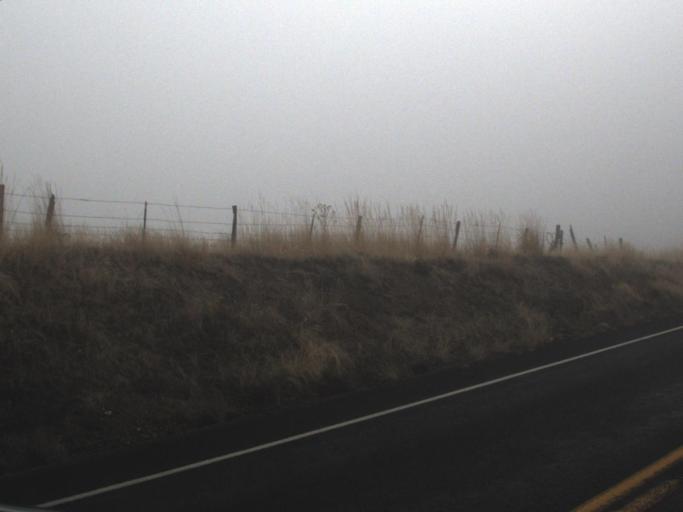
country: US
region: Washington
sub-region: Asotin County
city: Asotin
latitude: 46.3222
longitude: -117.0550
